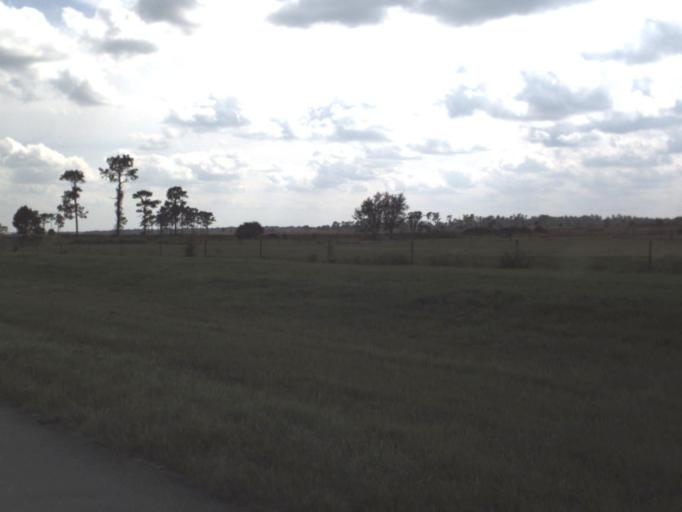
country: US
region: Florida
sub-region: Indian River County
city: Fellsmere
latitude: 27.6311
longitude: -80.8678
